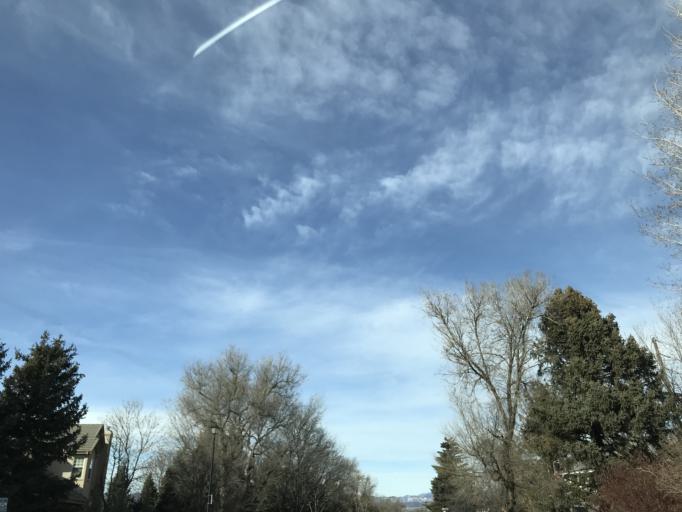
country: US
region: Colorado
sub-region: Arapahoe County
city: Littleton
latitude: 39.5969
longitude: -105.0085
